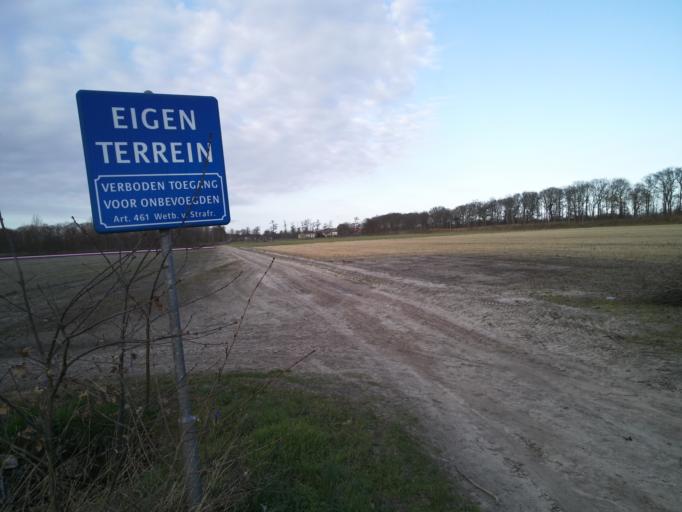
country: NL
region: South Holland
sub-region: Gemeente Teylingen
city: Sassenheim
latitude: 52.2500
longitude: 4.5288
